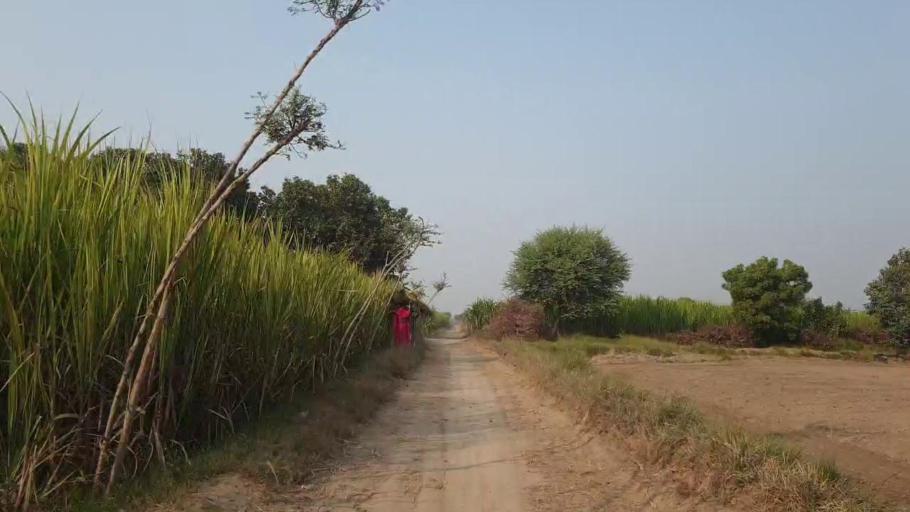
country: PK
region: Sindh
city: Tando Muhammad Khan
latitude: 25.1458
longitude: 68.6168
